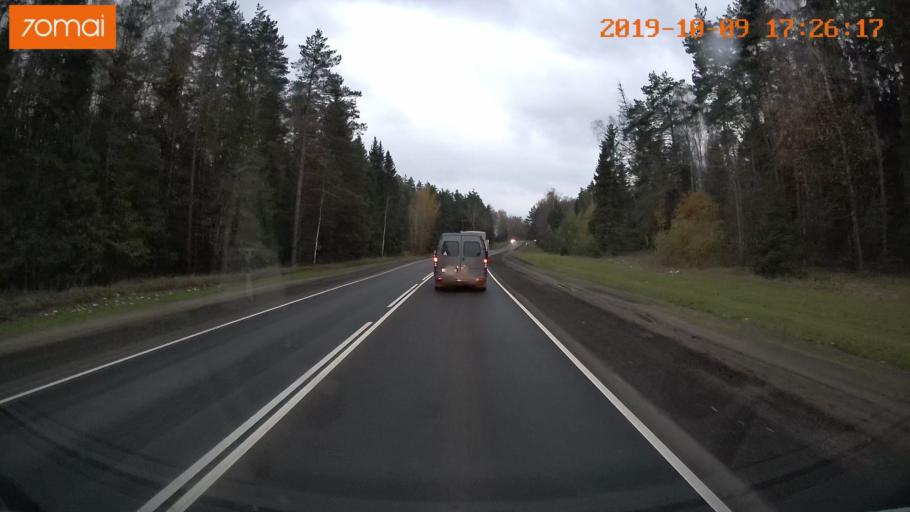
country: RU
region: Ivanovo
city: Furmanov
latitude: 57.1748
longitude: 41.0813
